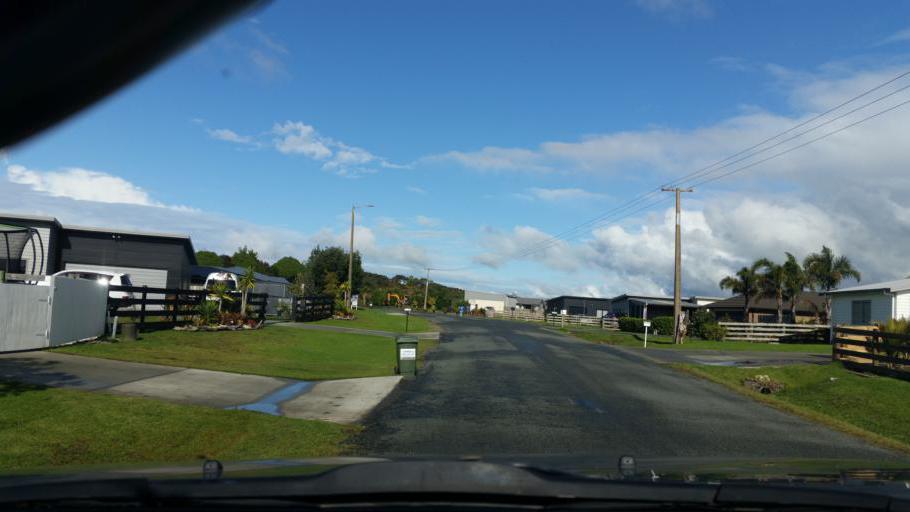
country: NZ
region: Auckland
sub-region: Auckland
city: Wellsford
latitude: -36.0931
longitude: 174.5740
